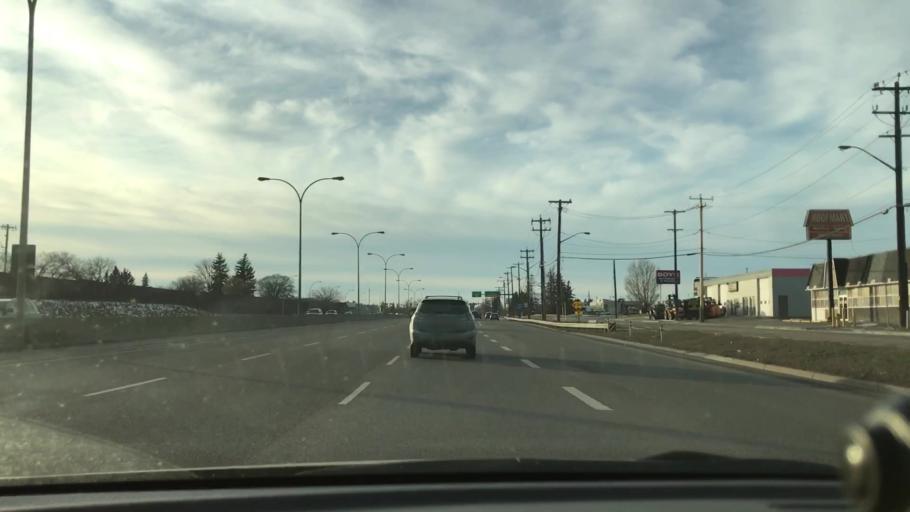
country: CA
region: Alberta
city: Edmonton
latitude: 53.5825
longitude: -113.4610
